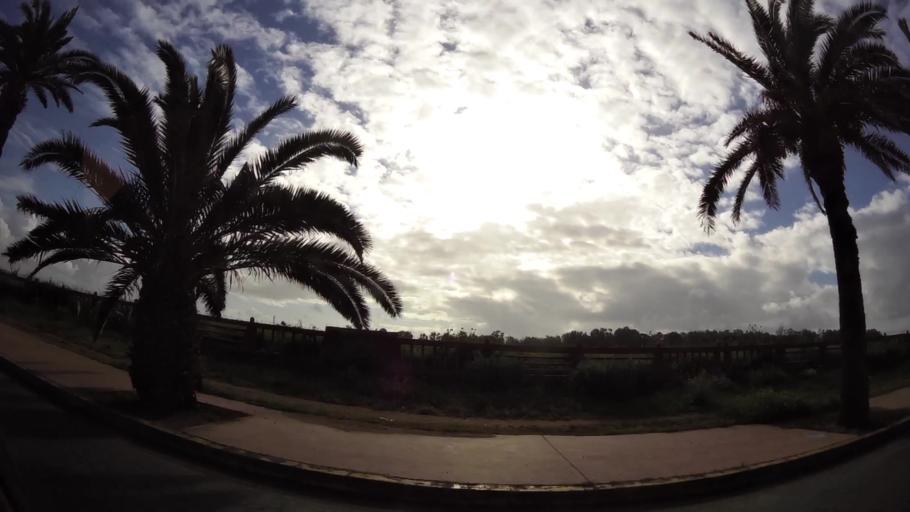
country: MA
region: Grand Casablanca
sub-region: Mohammedia
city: Mohammedia
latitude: 33.7036
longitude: -7.4008
